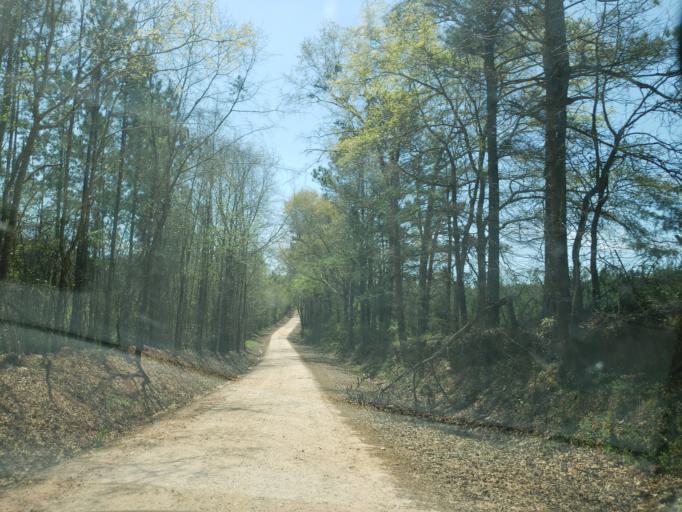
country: US
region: Alabama
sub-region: Tallapoosa County
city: Camp Hill
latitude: 32.6650
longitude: -85.6623
